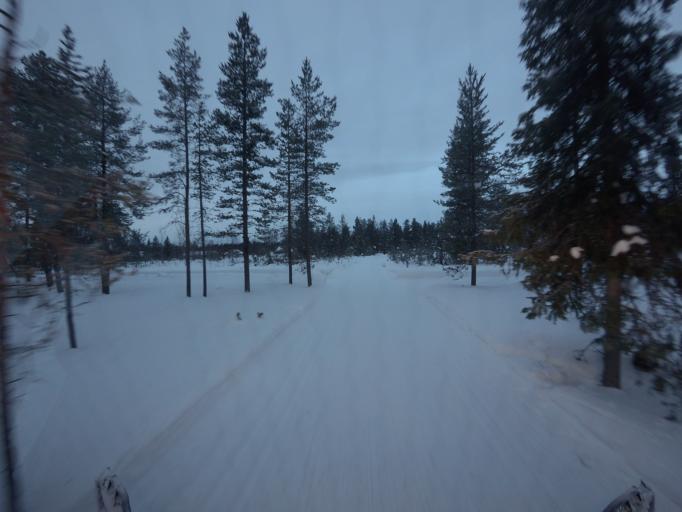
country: FI
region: Lapland
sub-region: Tunturi-Lappi
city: Kolari
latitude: 67.6244
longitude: 24.1658
